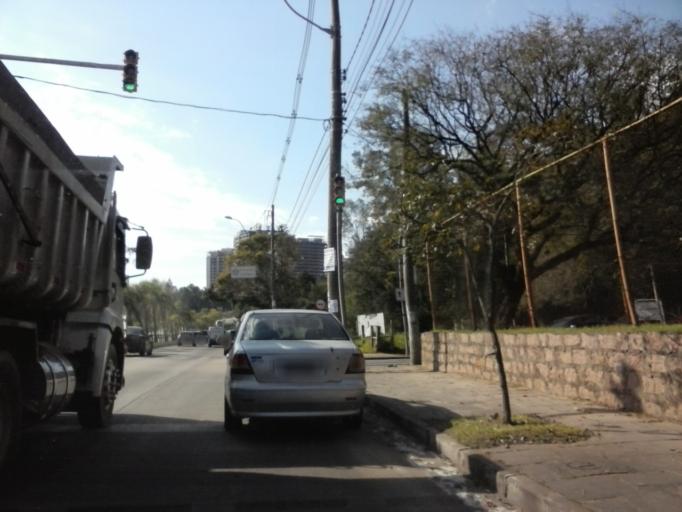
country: BR
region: Rio Grande do Sul
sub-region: Porto Alegre
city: Porto Alegre
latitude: -30.0475
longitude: -51.1783
